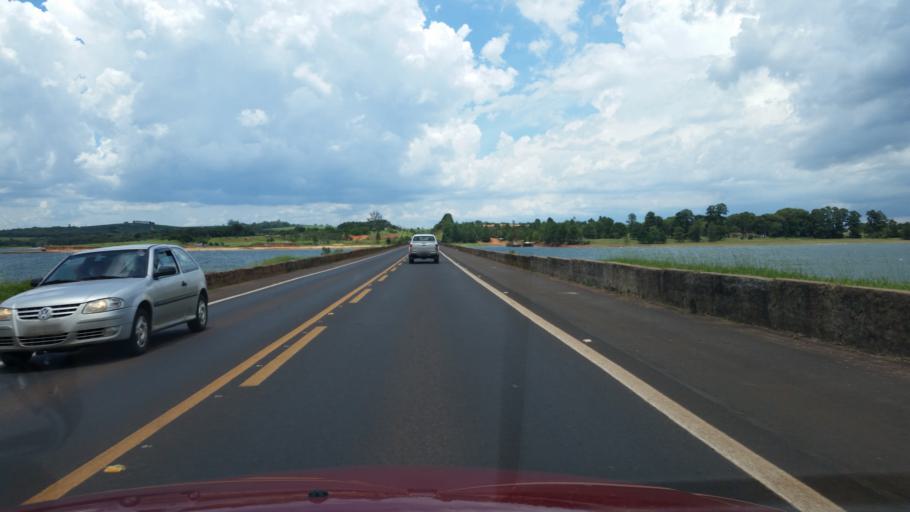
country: BR
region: Sao Paulo
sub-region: Itai
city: Itai
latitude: -23.2694
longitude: -49.0111
